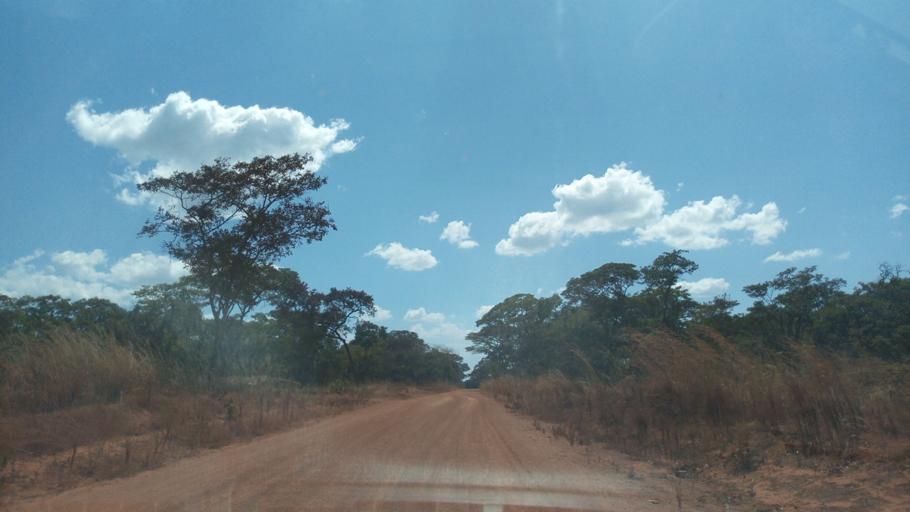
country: ZM
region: Luapula
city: Mwense
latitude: -10.6596
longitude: 28.1416
